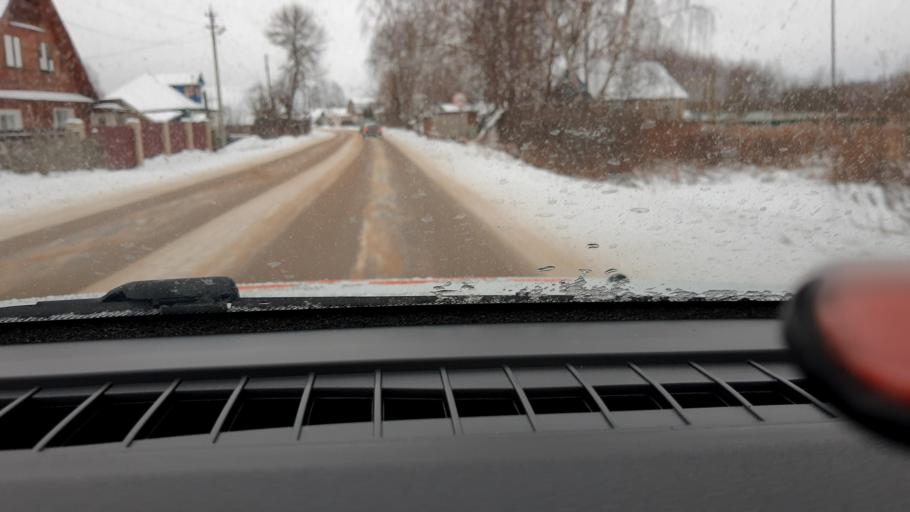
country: RU
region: Nizjnij Novgorod
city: Afonino
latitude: 56.3213
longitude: 44.1550
